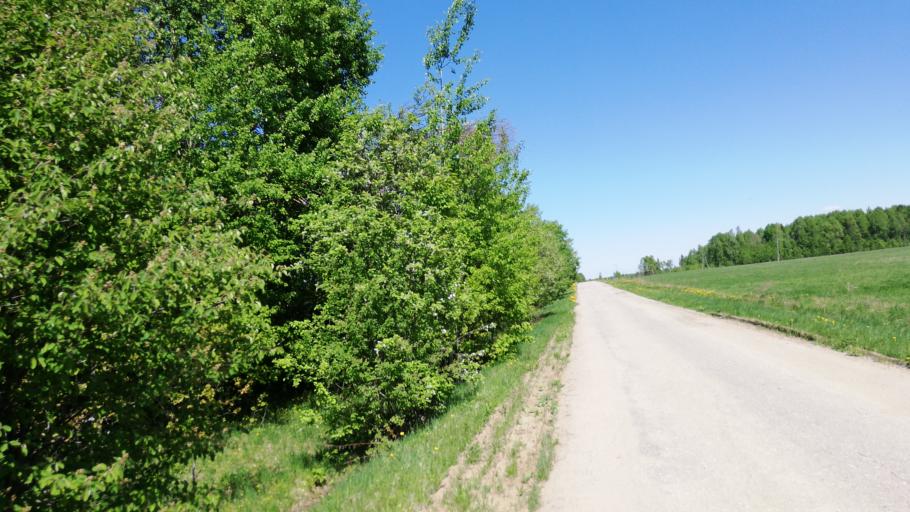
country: RU
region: Ivanovo
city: Pistsovo
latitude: 57.1191
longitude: 40.5978
